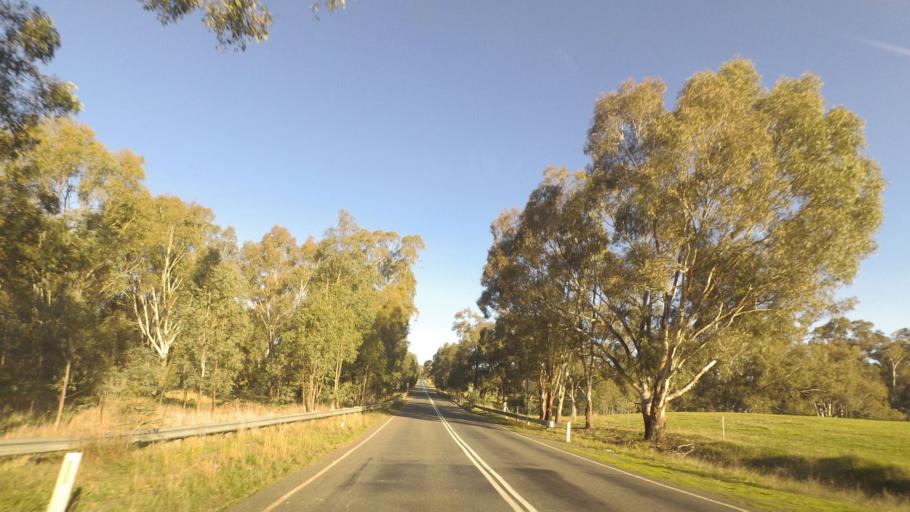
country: AU
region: Victoria
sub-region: Greater Bendigo
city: Epsom
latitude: -36.7472
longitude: 144.5106
